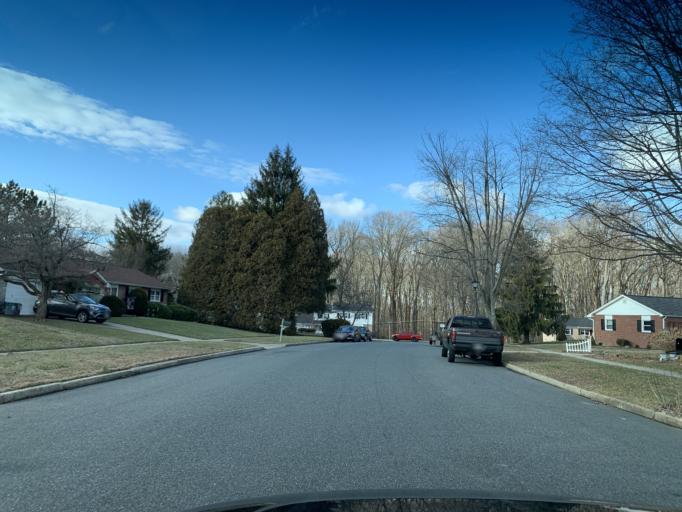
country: US
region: Maryland
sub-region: Harford County
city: South Bel Air
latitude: 39.5330
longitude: -76.3372
